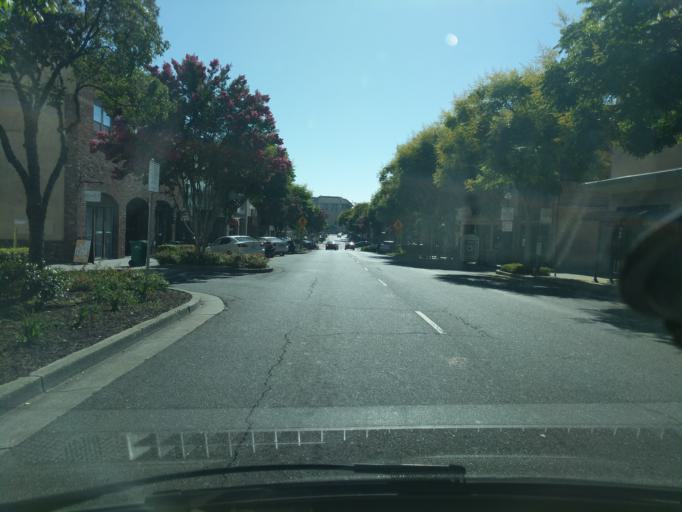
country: US
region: California
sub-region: Alameda County
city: Hayward
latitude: 37.6728
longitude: -122.0828
